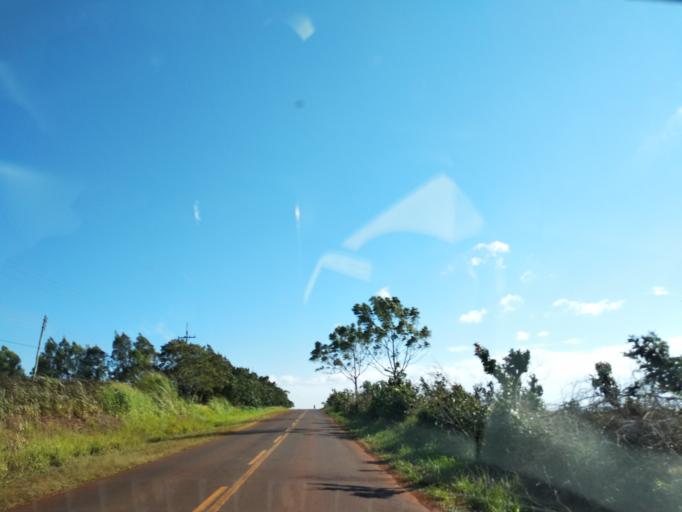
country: PY
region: Itapua
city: Hohenau
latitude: -27.0743
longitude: -55.7152
